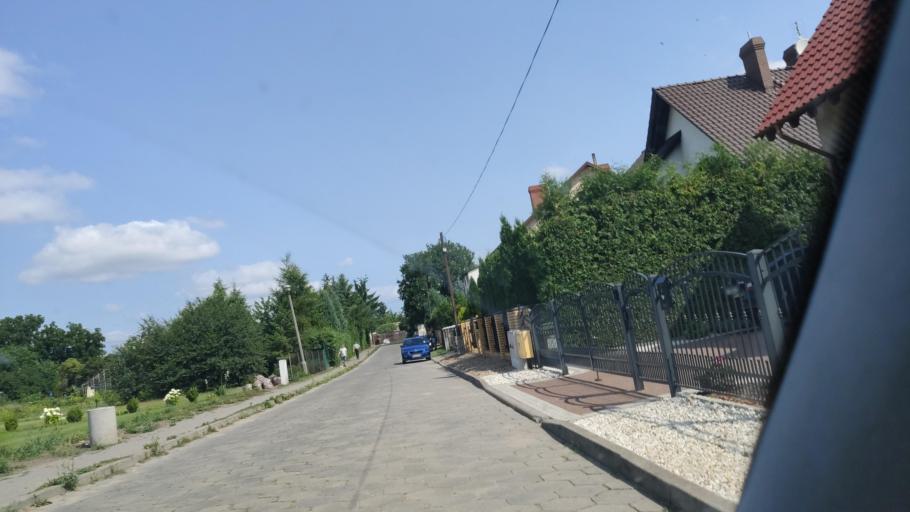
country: PL
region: Kujawsko-Pomorskie
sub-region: Powiat zninski
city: Znin
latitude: 52.8520
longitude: 17.7520
